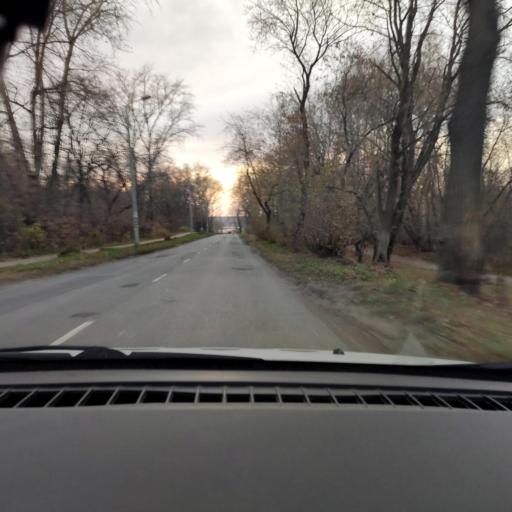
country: RU
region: Perm
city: Perm
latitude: 58.1211
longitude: 56.3751
